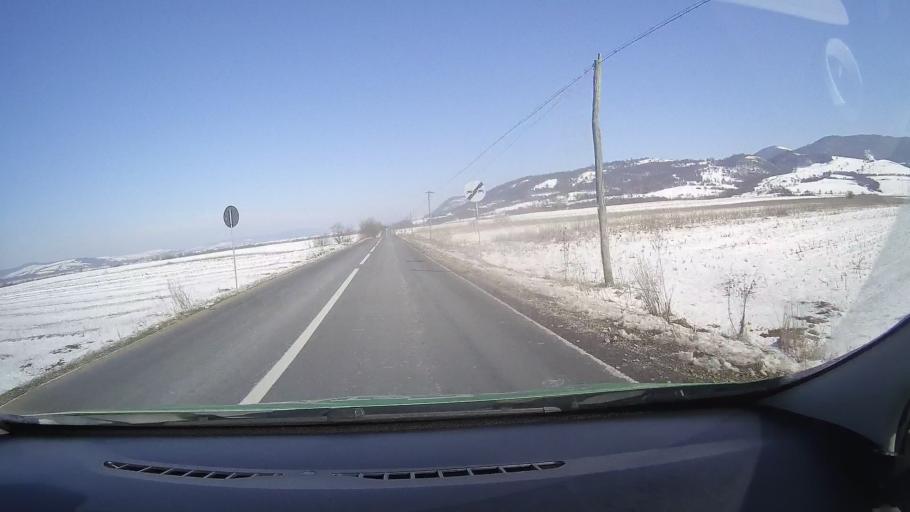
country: RO
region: Brasov
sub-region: Comuna Comana
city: Comana de Jos
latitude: 45.9215
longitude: 25.2393
